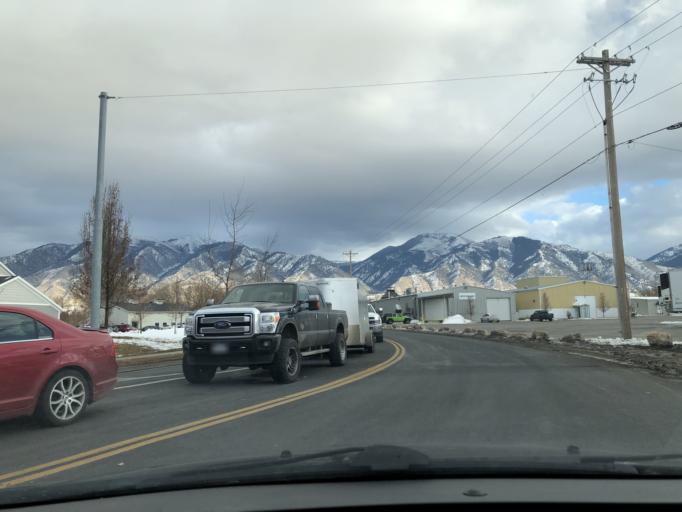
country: US
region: Utah
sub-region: Cache County
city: Nibley
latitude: 41.7032
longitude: -111.8514
